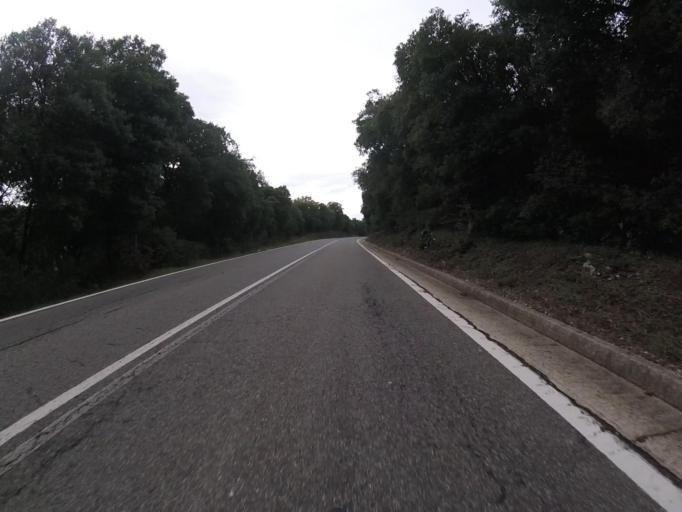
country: ES
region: Navarre
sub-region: Provincia de Navarra
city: Lezaun
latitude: 42.7466
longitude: -2.0167
